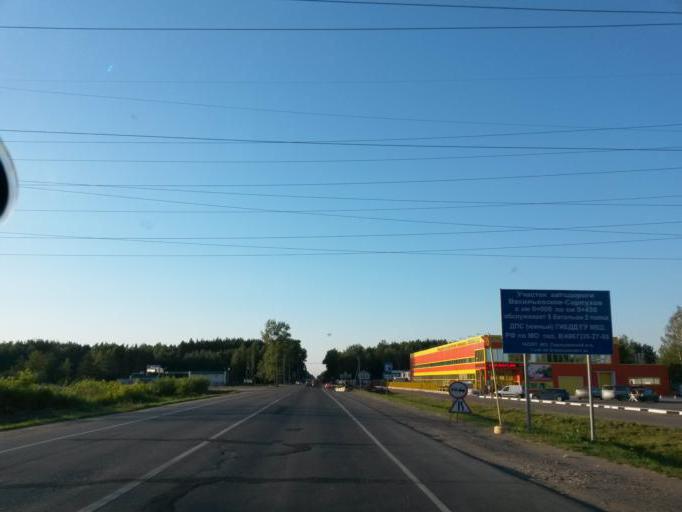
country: RU
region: Moskovskaya
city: Serpukhov
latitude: 54.9531
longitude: 37.4097
